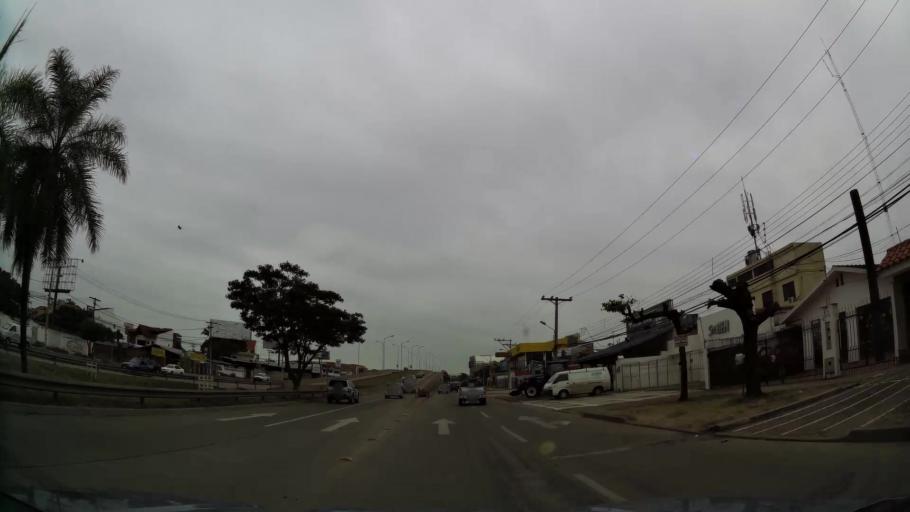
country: BO
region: Santa Cruz
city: Santa Cruz de la Sierra
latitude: -17.7506
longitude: -63.1725
